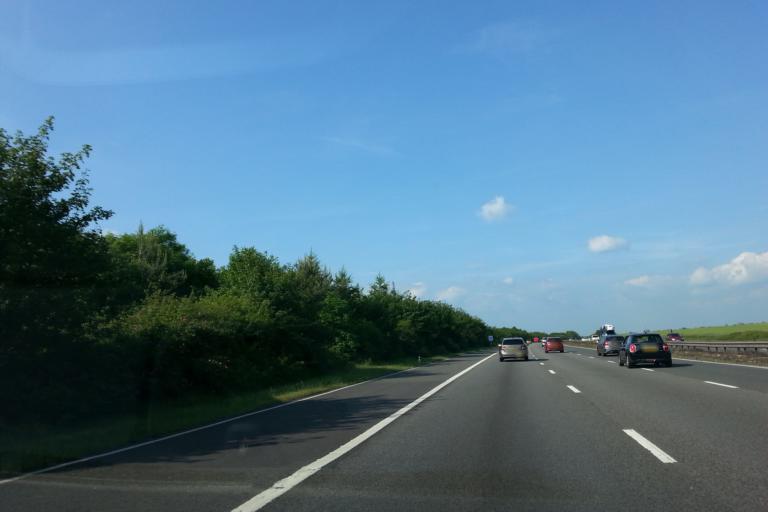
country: GB
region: England
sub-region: Leicestershire
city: Hinckley
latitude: 52.4799
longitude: -1.3997
